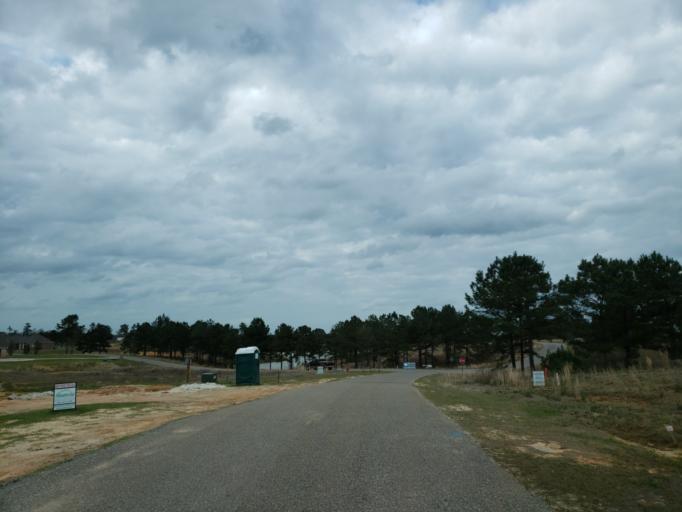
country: US
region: Mississippi
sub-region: Jones County
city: Ellisville
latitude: 31.5529
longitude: -89.2549
